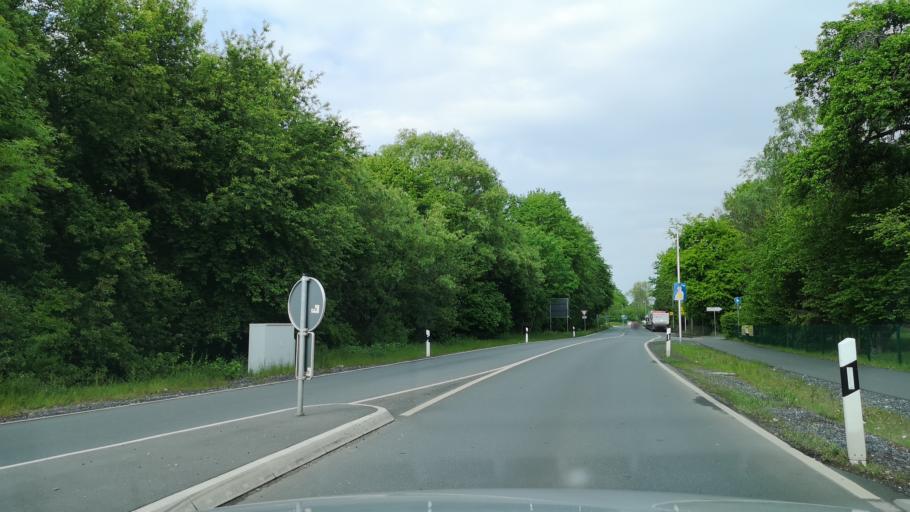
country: DE
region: North Rhine-Westphalia
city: Iserlohn
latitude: 51.4204
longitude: 7.7105
